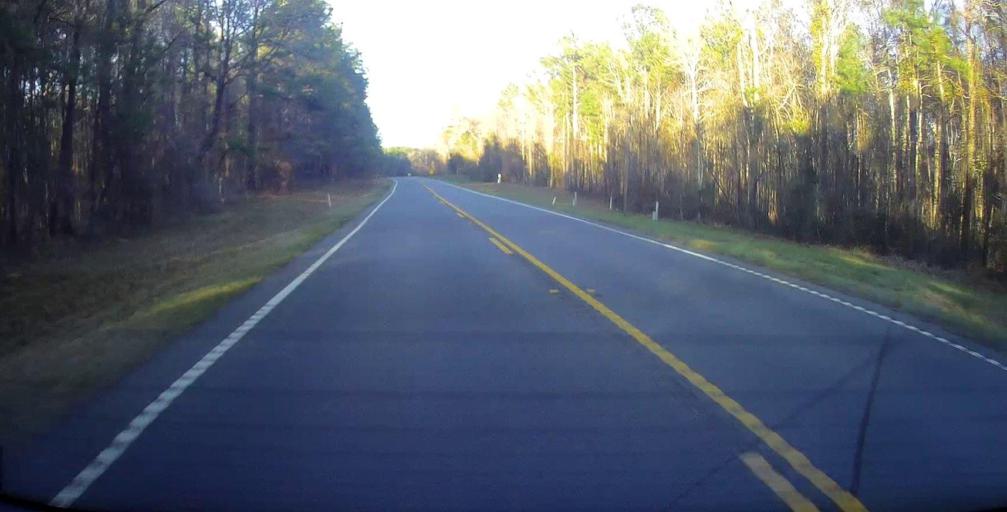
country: US
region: Georgia
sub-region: Talbot County
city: Talbotton
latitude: 32.6790
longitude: -84.6012
